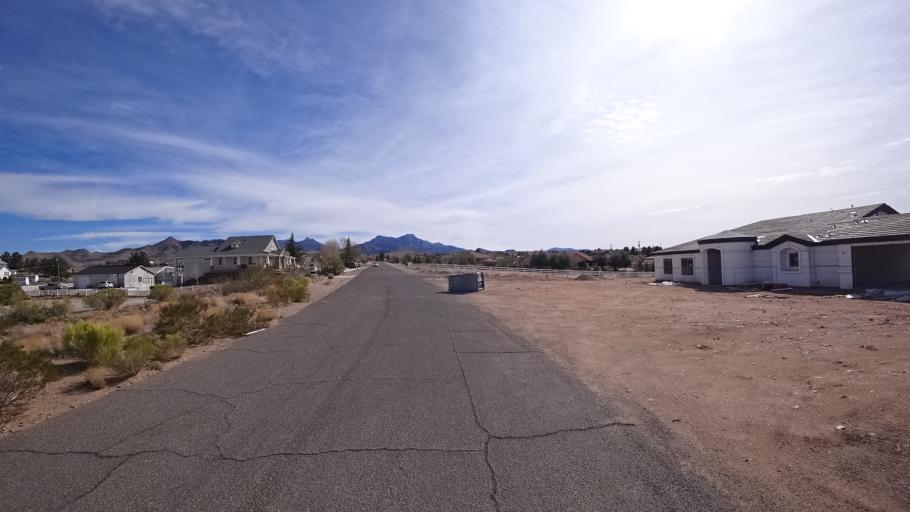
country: US
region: Arizona
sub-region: Mohave County
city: Kingman
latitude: 35.1921
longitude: -113.9899
